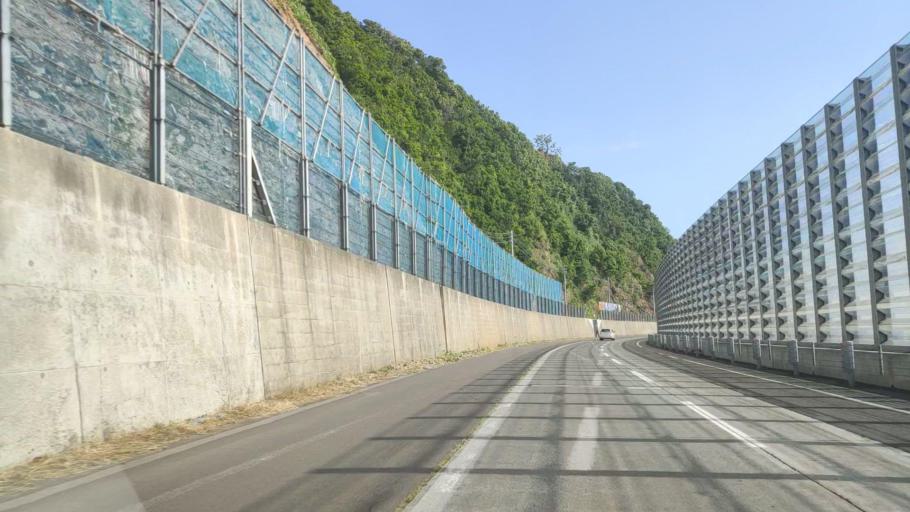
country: JP
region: Hokkaido
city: Rumoi
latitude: 43.6626
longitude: 141.3501
